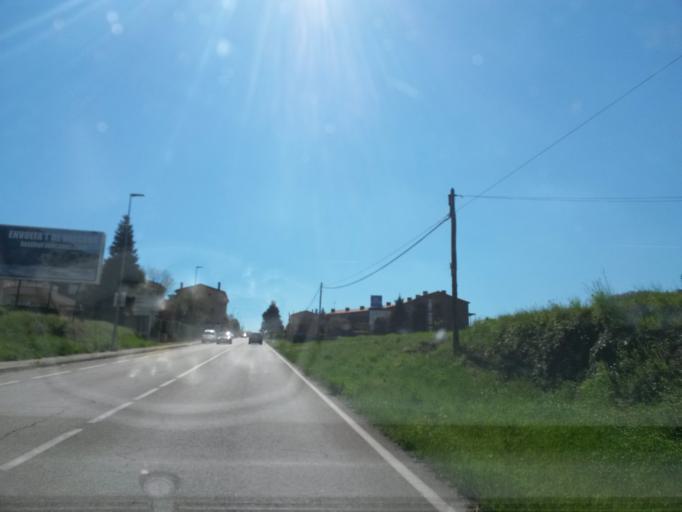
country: ES
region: Catalonia
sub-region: Provincia de Girona
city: Olot
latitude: 42.1751
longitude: 2.4927
